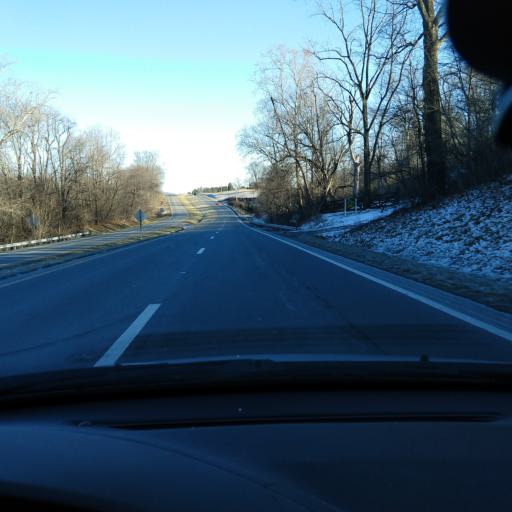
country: US
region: Virginia
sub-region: Botetourt County
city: Blue Ridge
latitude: 37.3615
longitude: -79.6815
